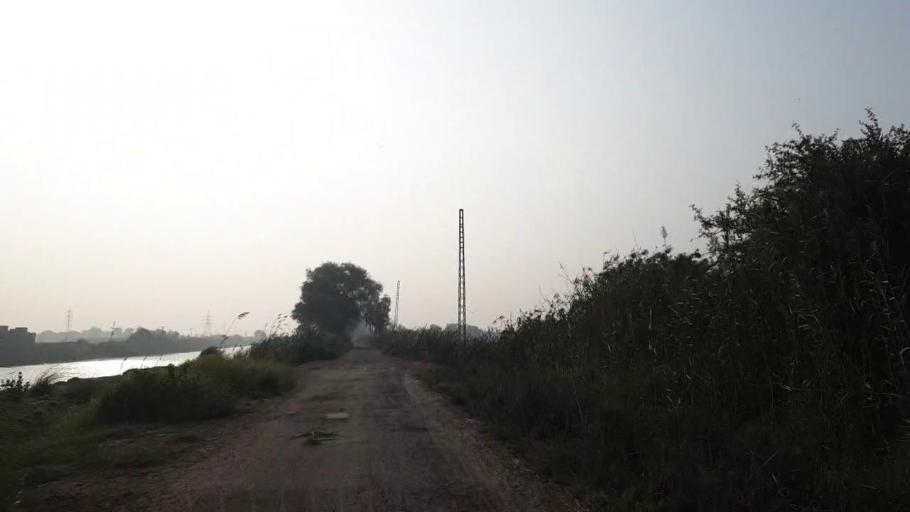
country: PK
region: Sindh
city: Tando Muhammad Khan
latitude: 25.1230
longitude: 68.5628
